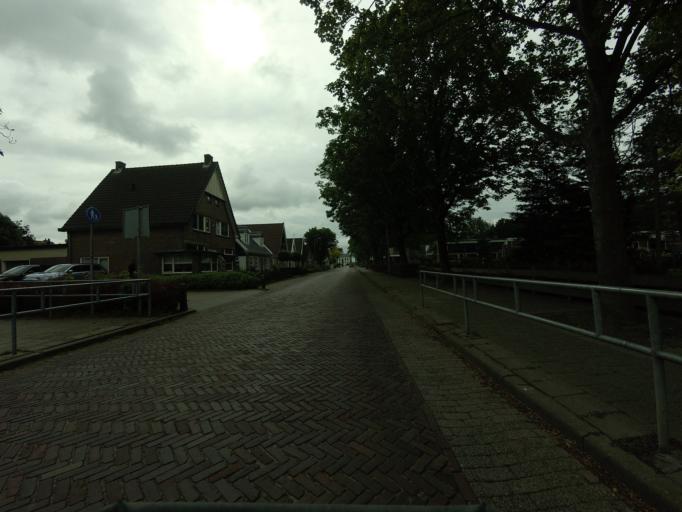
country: NL
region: North Holland
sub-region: Gemeente Hoorn
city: Hoorn
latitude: 52.6915
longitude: 5.0578
